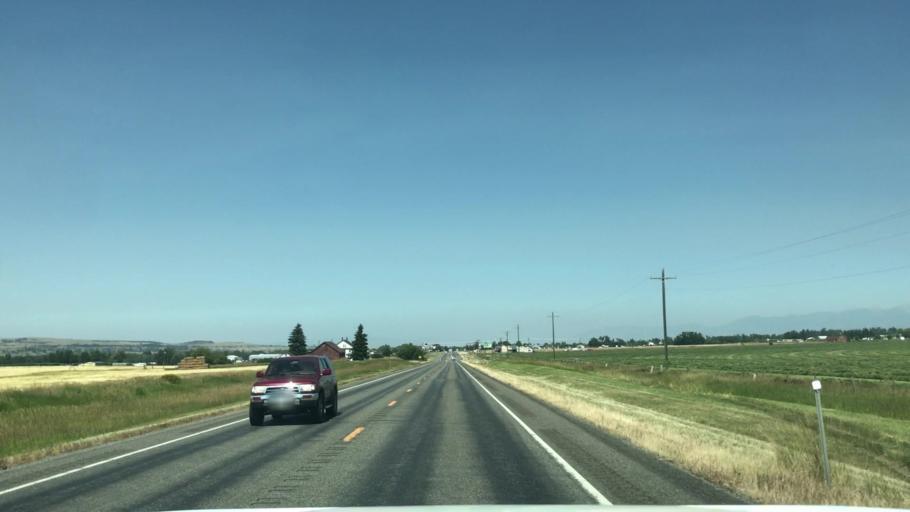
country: US
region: Montana
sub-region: Gallatin County
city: Four Corners
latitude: 45.5767
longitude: -111.1969
